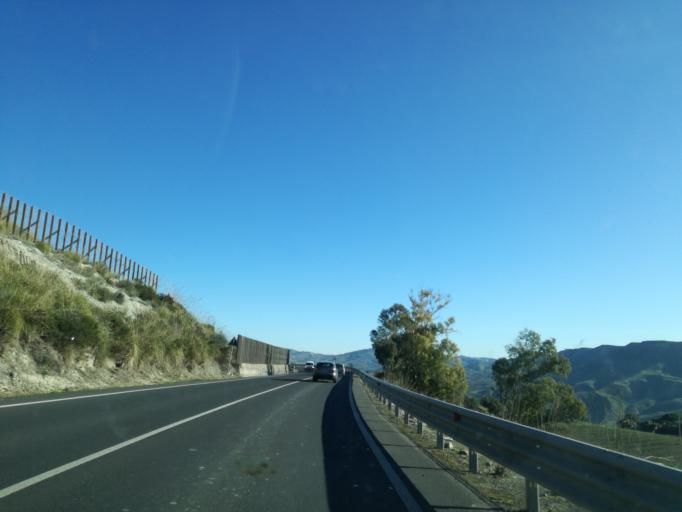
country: IT
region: Sicily
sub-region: Catania
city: San Michele di Ganzaria
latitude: 37.2171
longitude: 14.4231
